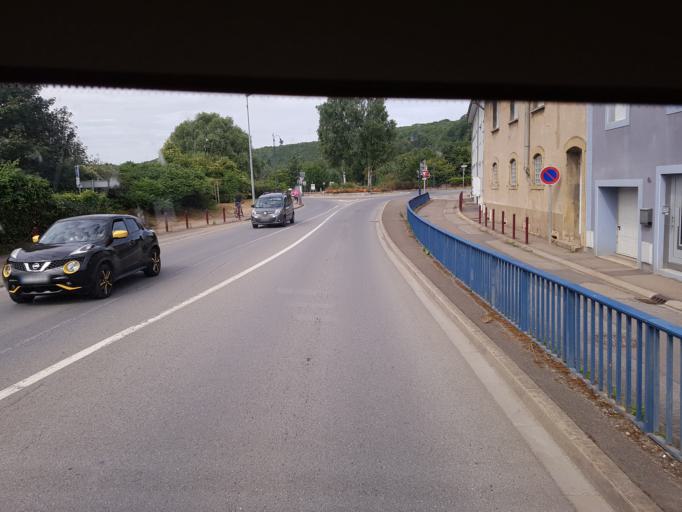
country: FR
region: Lorraine
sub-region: Departement de la Moselle
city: Moyeuvre-Grande
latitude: 49.2493
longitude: 6.0449
